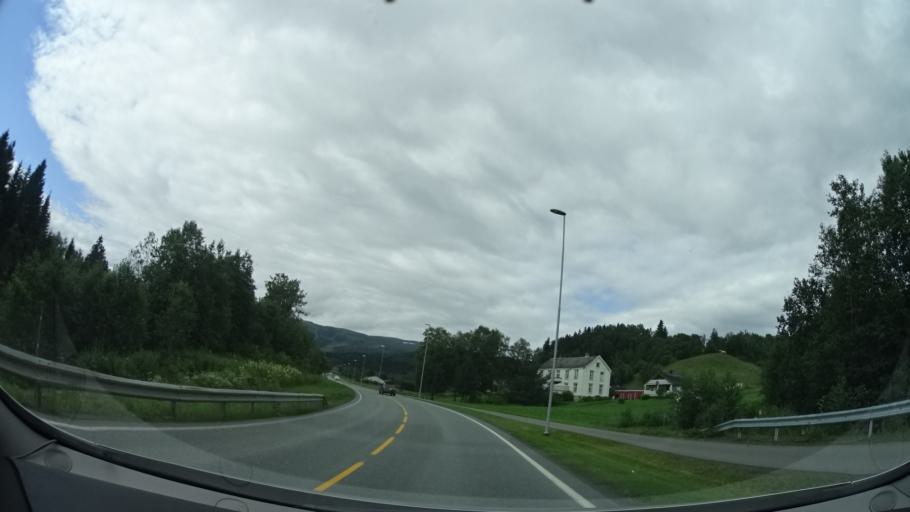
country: NO
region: Nord-Trondelag
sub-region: Meraker
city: Meraker
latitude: 63.4236
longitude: 11.7343
